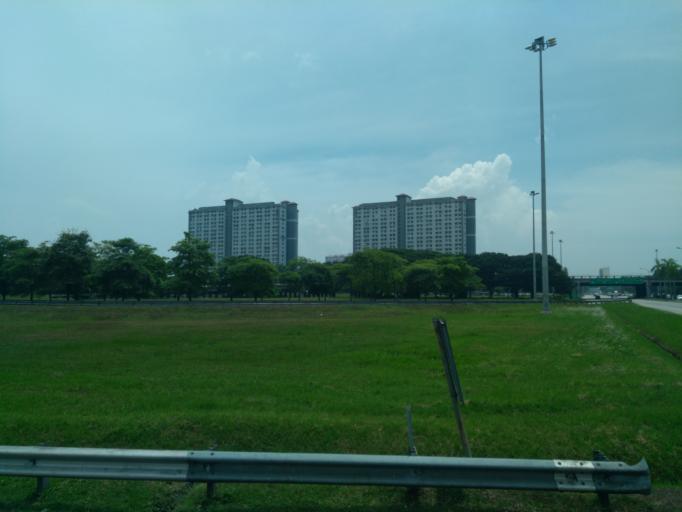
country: MY
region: Penang
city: Perai
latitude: 5.3750
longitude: 100.4047
